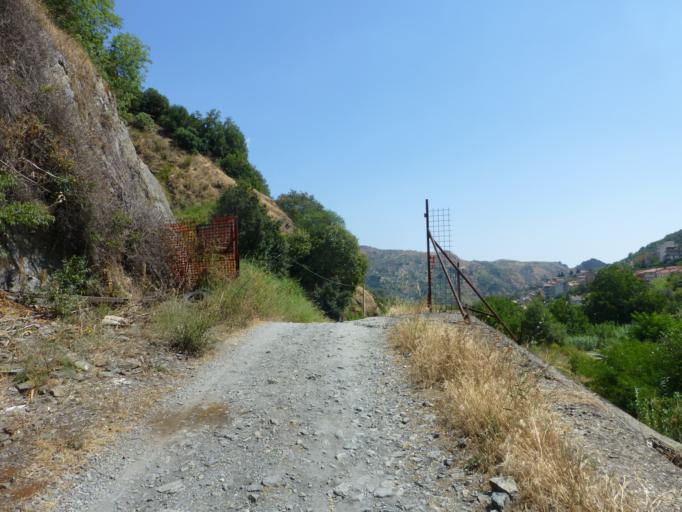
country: IT
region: Calabria
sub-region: Provincia di Reggio Calabria
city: Pazzano
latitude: 38.4781
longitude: 16.4439
